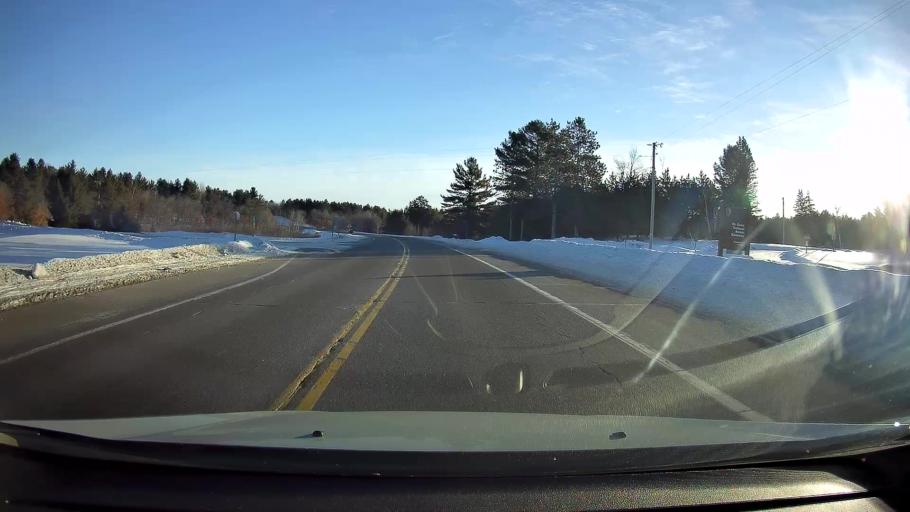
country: US
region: Wisconsin
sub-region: Washburn County
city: Spooner
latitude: 45.9051
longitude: -91.8162
